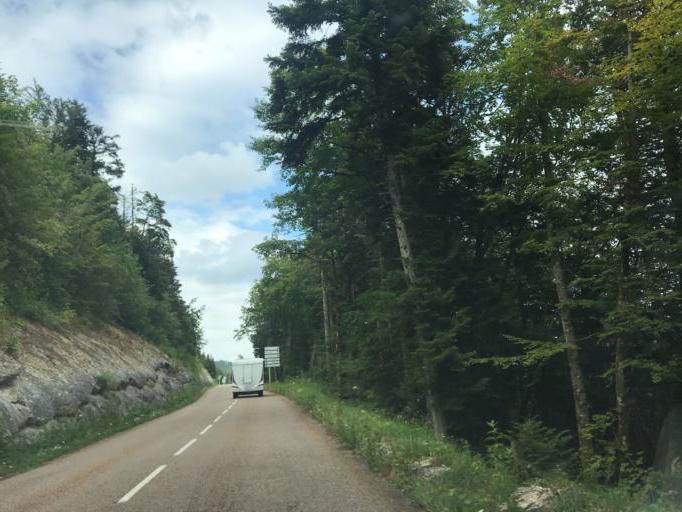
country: FR
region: Franche-Comte
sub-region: Departement du Jura
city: Longchaumois
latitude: 46.4947
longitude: 5.9225
